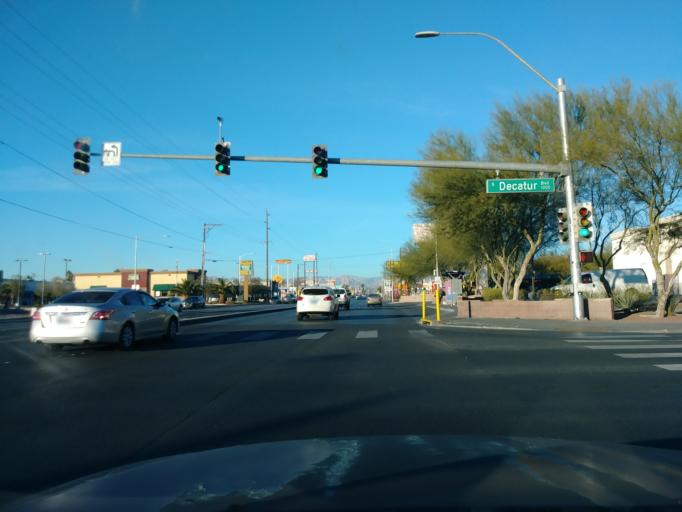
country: US
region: Nevada
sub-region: Clark County
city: Spring Valley
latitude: 36.1592
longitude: -115.2059
